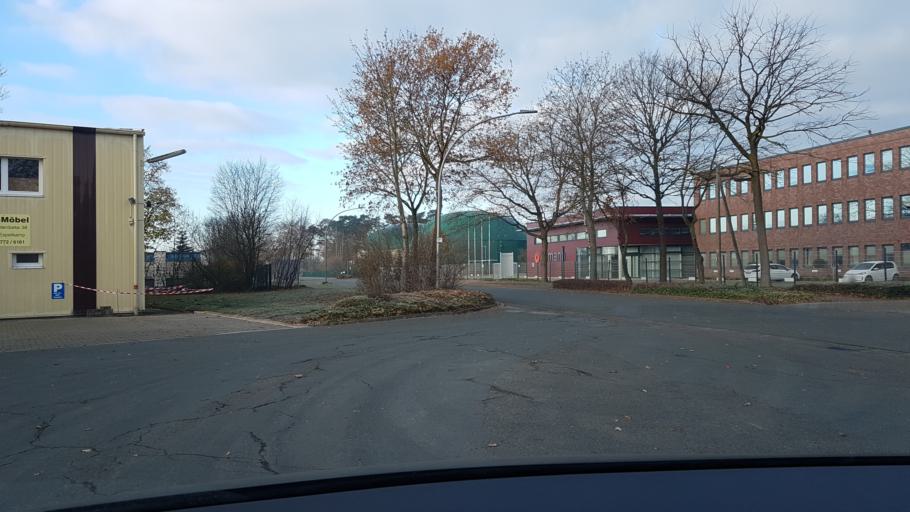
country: DE
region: North Rhine-Westphalia
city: Espelkamp
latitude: 52.3932
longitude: 8.6255
